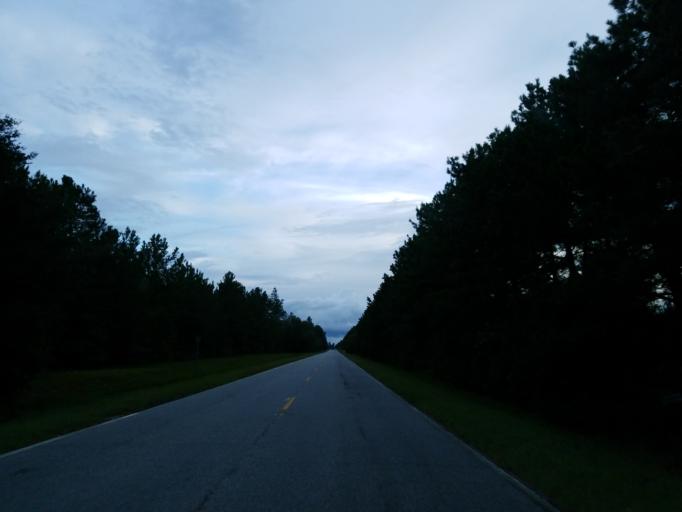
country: US
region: Georgia
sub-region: Echols County
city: Statenville
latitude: 30.6323
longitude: -83.0243
